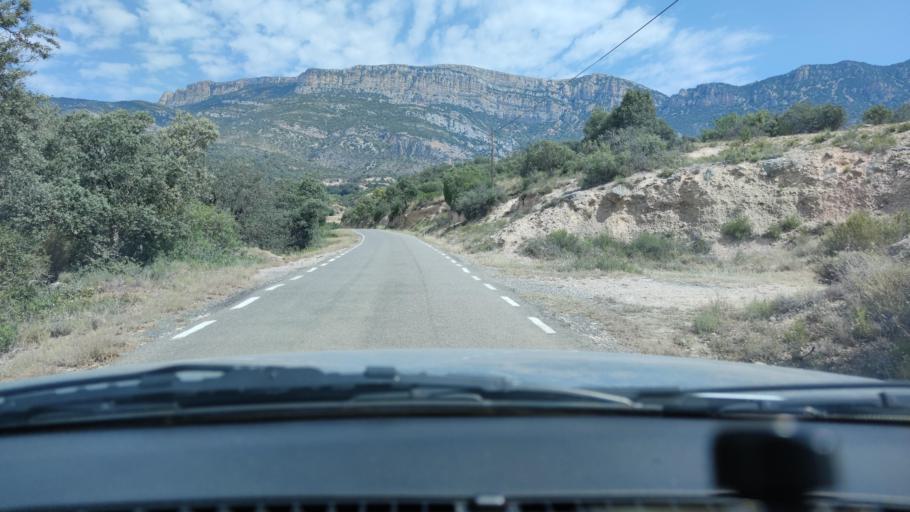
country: ES
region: Catalonia
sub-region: Provincia de Lleida
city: Ager
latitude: 42.0097
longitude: 0.8320
